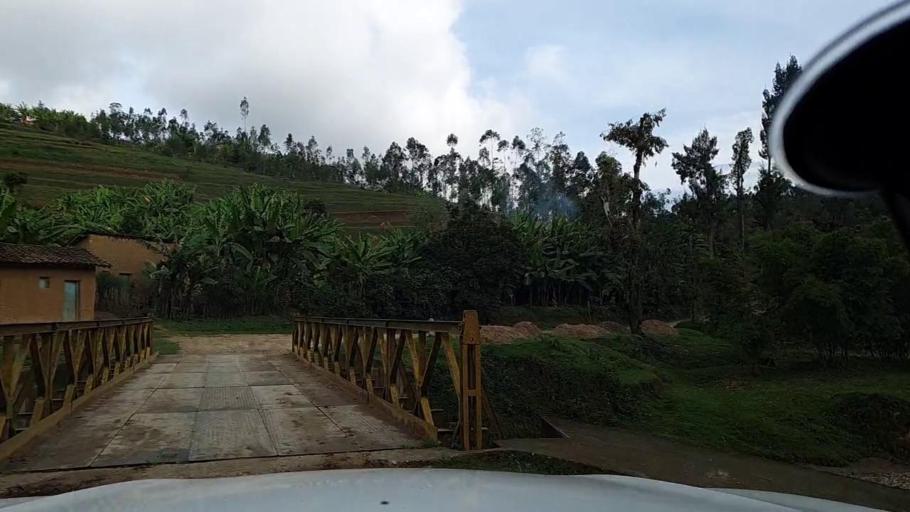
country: RW
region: Western Province
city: Kibuye
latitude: -2.1529
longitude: 29.5388
